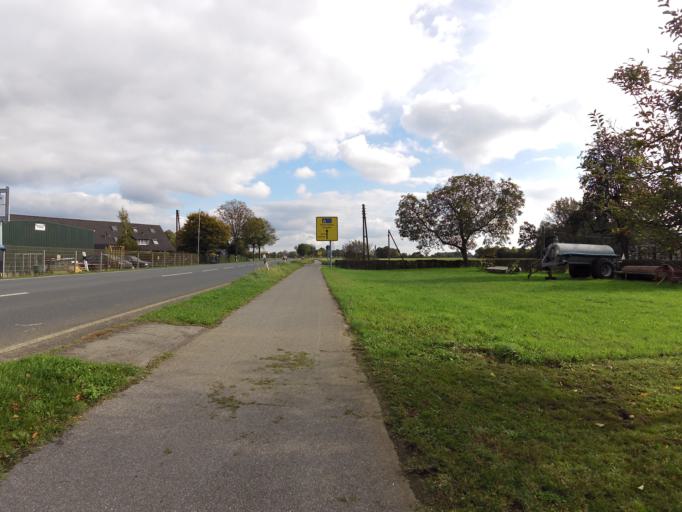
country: DE
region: North Rhine-Westphalia
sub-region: Regierungsbezirk Dusseldorf
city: Mehrhoog
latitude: 51.7768
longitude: 6.5534
